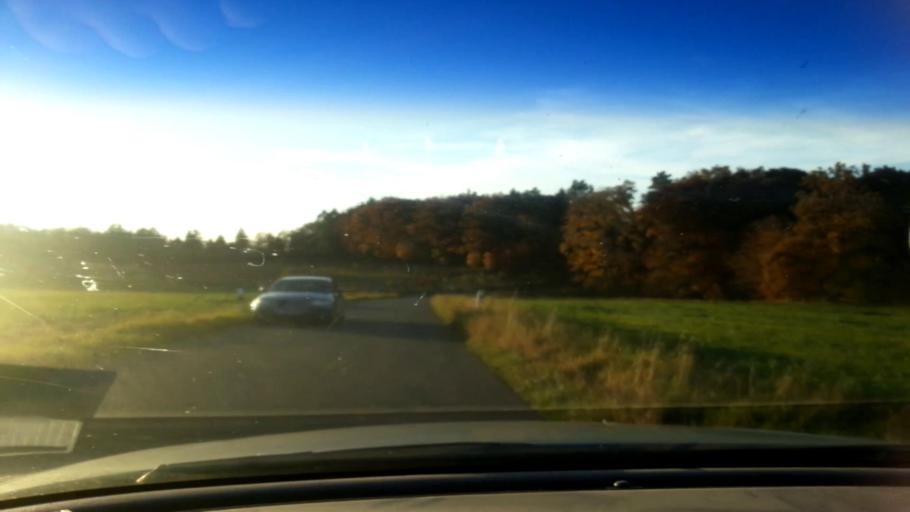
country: DE
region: Bavaria
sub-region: Upper Franconia
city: Unterleinleiter
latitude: 49.8376
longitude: 11.2035
